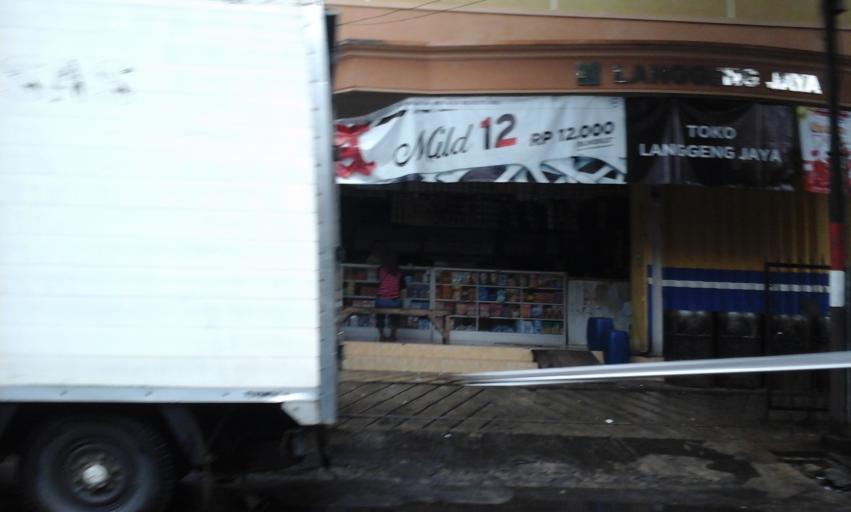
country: ID
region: East Java
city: Lumajang
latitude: -8.1292
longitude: 113.2236
